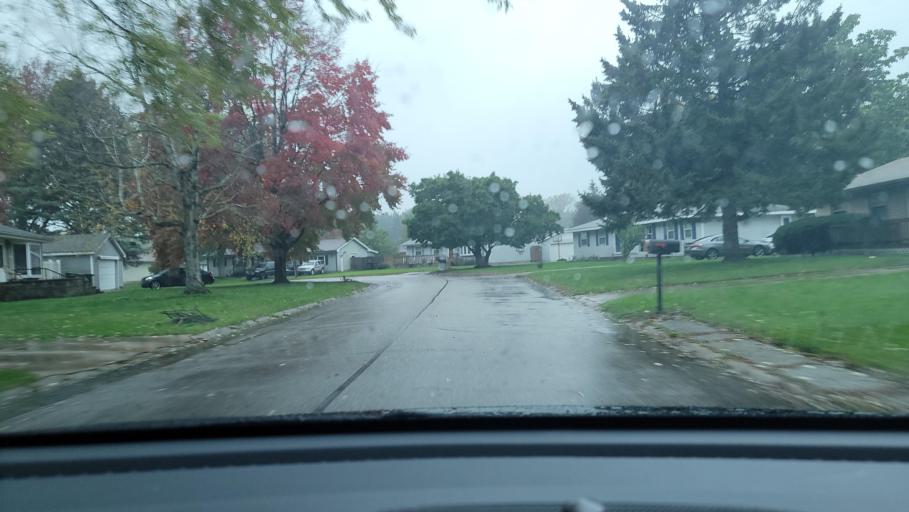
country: US
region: Indiana
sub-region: Porter County
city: Portage
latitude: 41.5859
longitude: -87.1909
